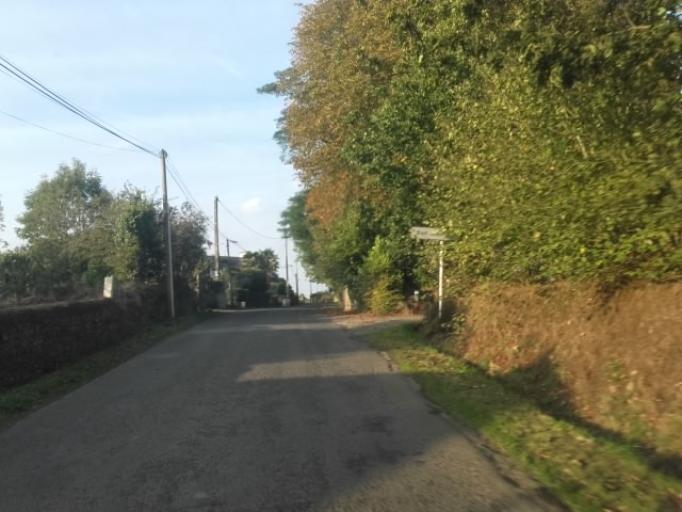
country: FR
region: Brittany
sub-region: Departement des Cotes-d'Armor
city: Pleguien
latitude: 48.6414
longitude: -2.9400
